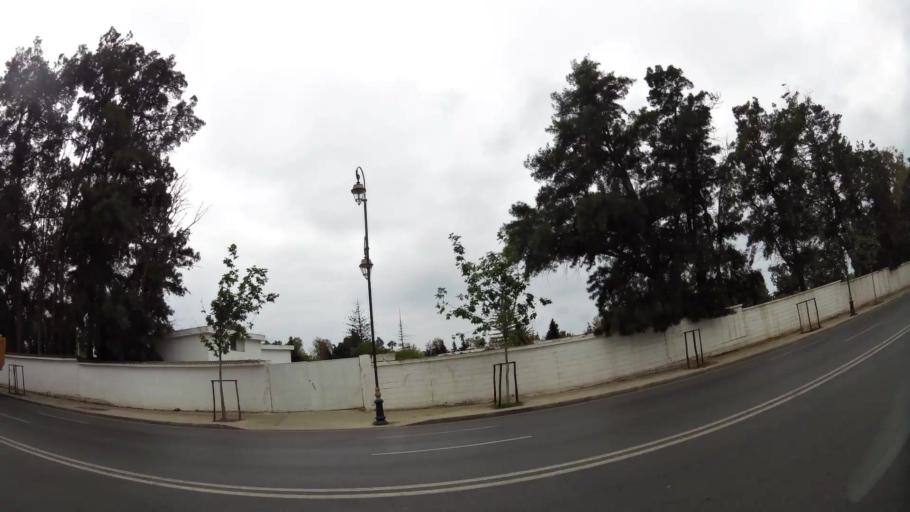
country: MA
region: Rabat-Sale-Zemmour-Zaer
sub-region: Rabat
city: Rabat
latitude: 33.9606
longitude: -6.8196
